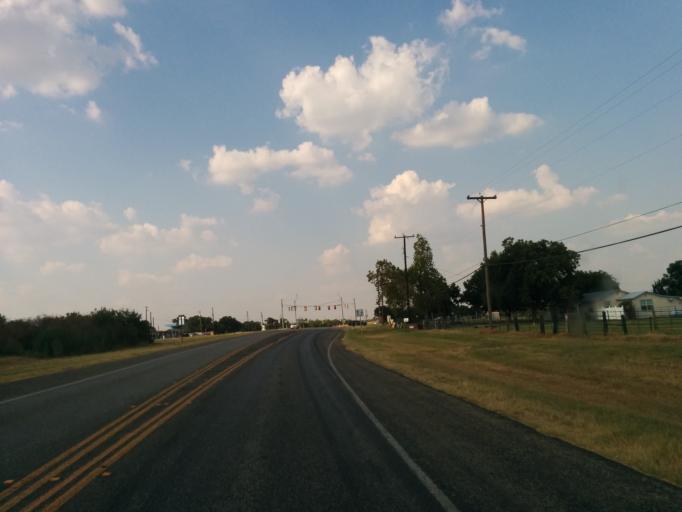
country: US
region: Texas
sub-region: Bexar County
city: Elmendorf
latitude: 29.3267
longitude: -98.2599
